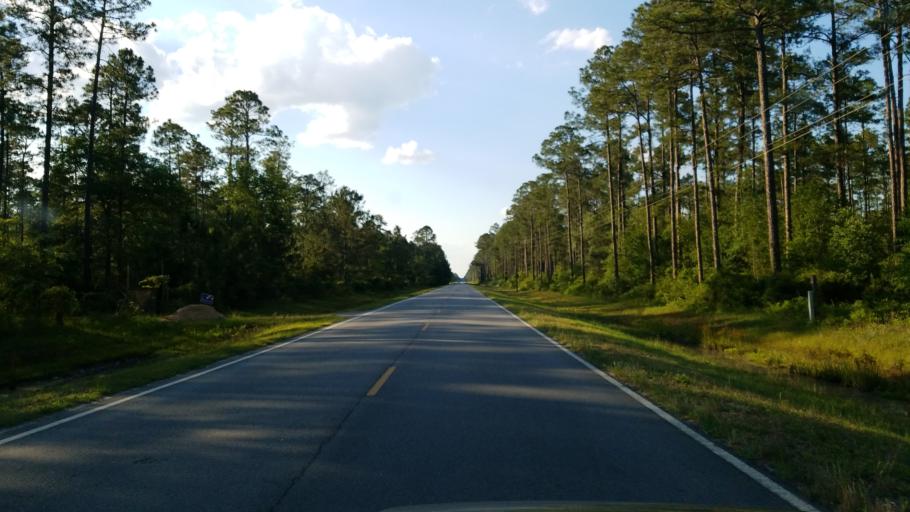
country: US
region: Georgia
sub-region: Lanier County
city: Lakeland
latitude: 31.0893
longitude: -83.0770
